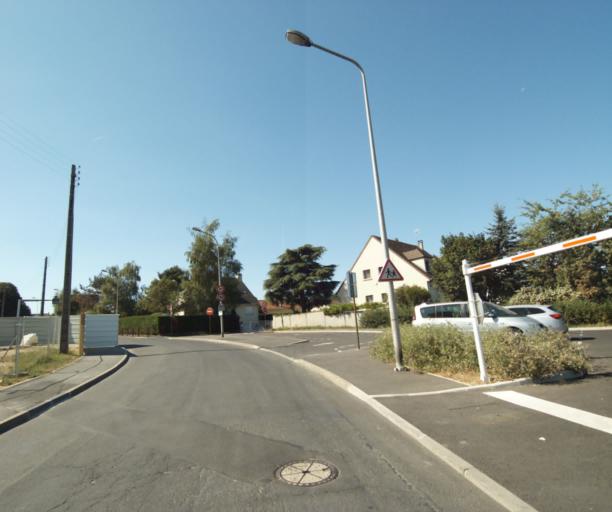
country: FR
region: Ile-de-France
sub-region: Departement de Seine-et-Marne
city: Gouvernes
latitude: 48.8736
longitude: 2.6952
